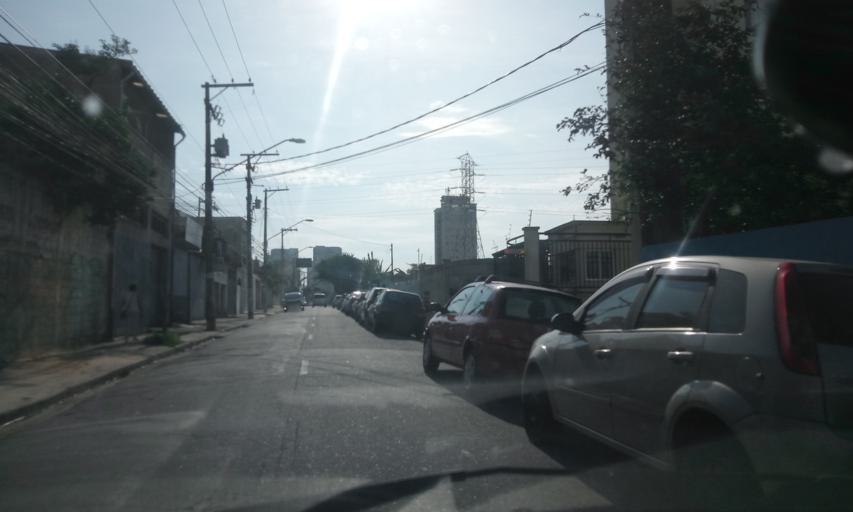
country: BR
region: Sao Paulo
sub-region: Sao Bernardo Do Campo
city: Sao Bernardo do Campo
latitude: -23.7067
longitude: -46.5359
